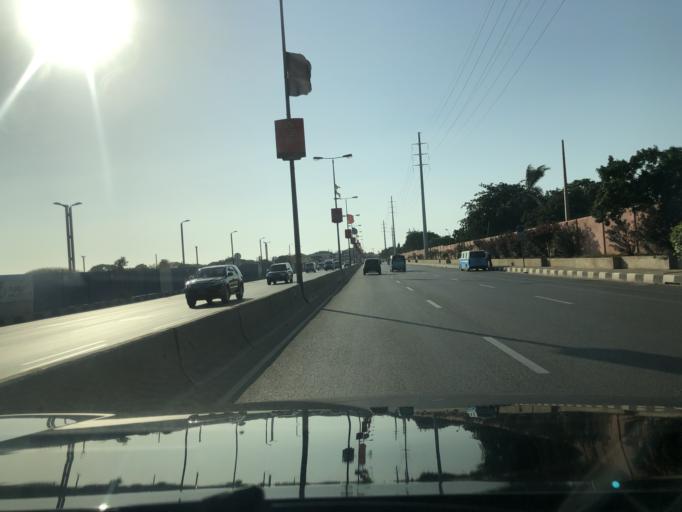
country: AO
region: Luanda
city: Luanda
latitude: -8.9068
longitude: 13.1794
